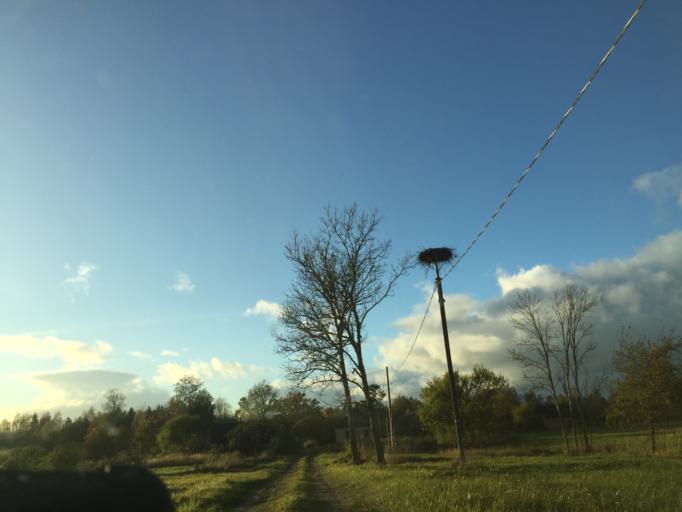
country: LV
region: Talsu Rajons
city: Sabile
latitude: 56.8991
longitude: 22.4008
